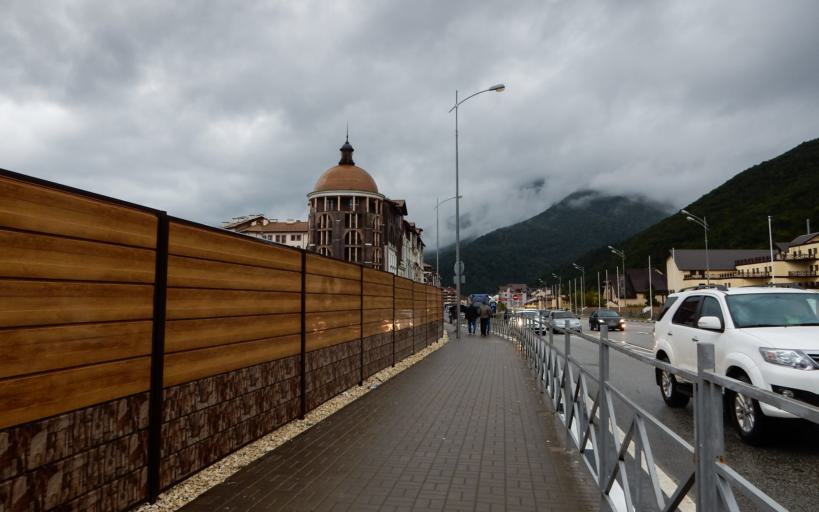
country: RU
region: Krasnodarskiy
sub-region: Sochi City
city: Krasnaya Polyana
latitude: 43.6823
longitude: 40.2718
